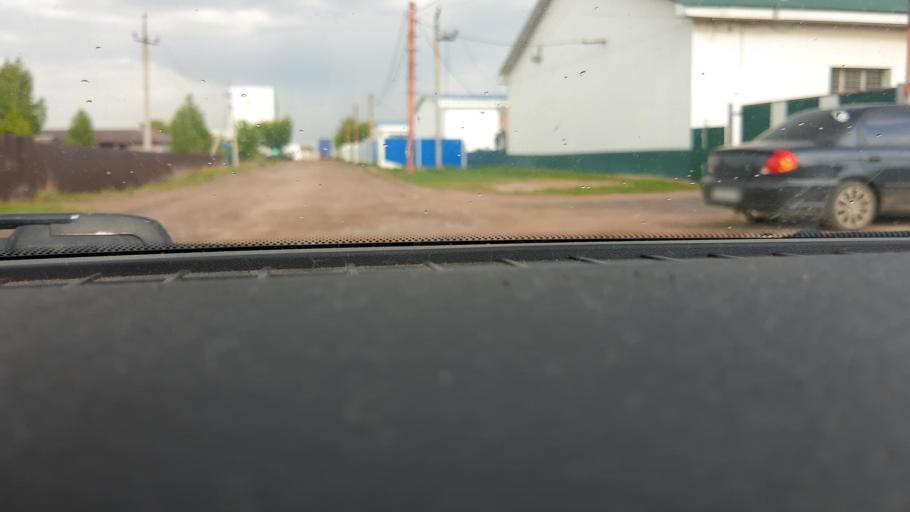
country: RU
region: Bashkortostan
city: Avdon
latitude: 54.6013
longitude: 55.8223
